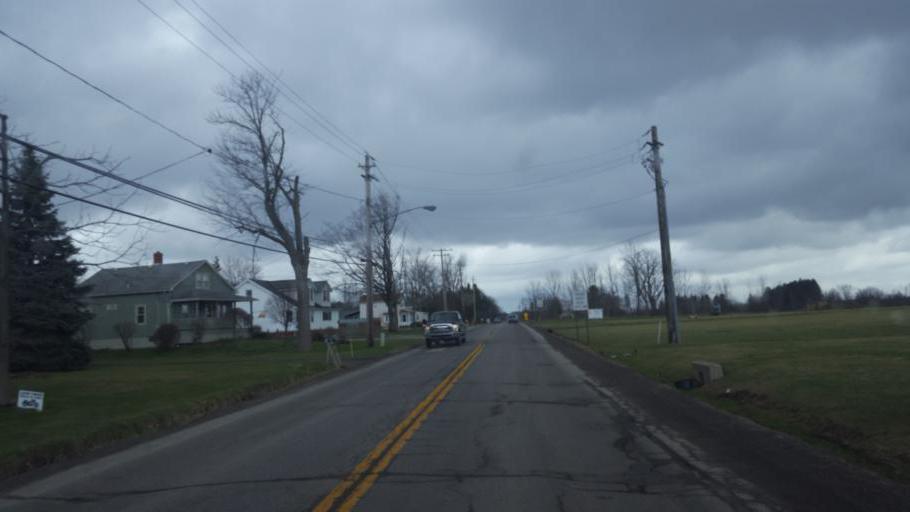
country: US
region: Ohio
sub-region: Geauga County
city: Middlefield
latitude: 41.4674
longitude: -81.0747
